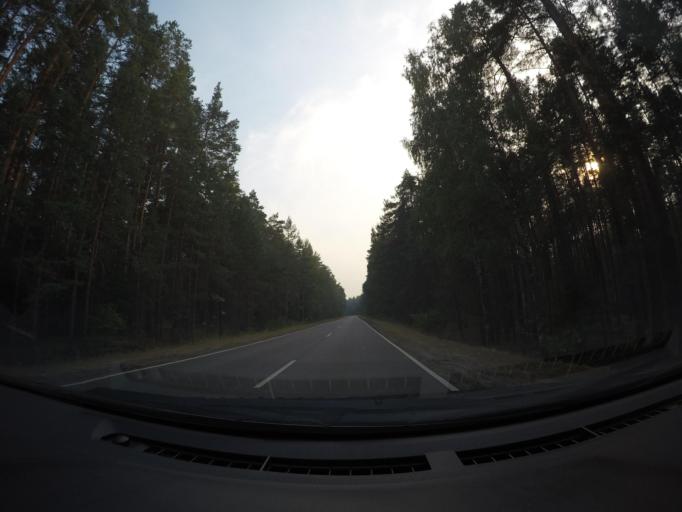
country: RU
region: Moskovskaya
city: Imeni Tsyurupy
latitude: 55.5119
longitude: 38.7203
